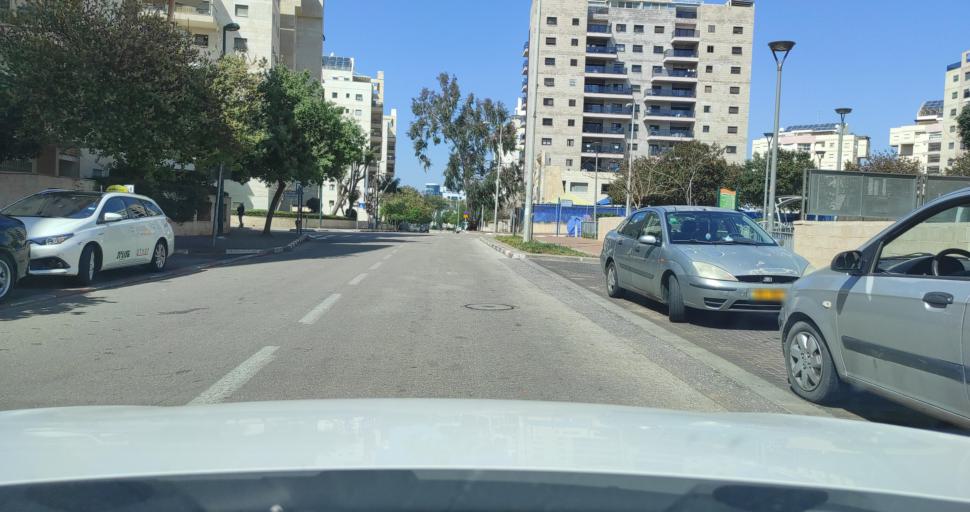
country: IL
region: Central District
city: Nordiyya
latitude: 32.3078
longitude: 34.8730
